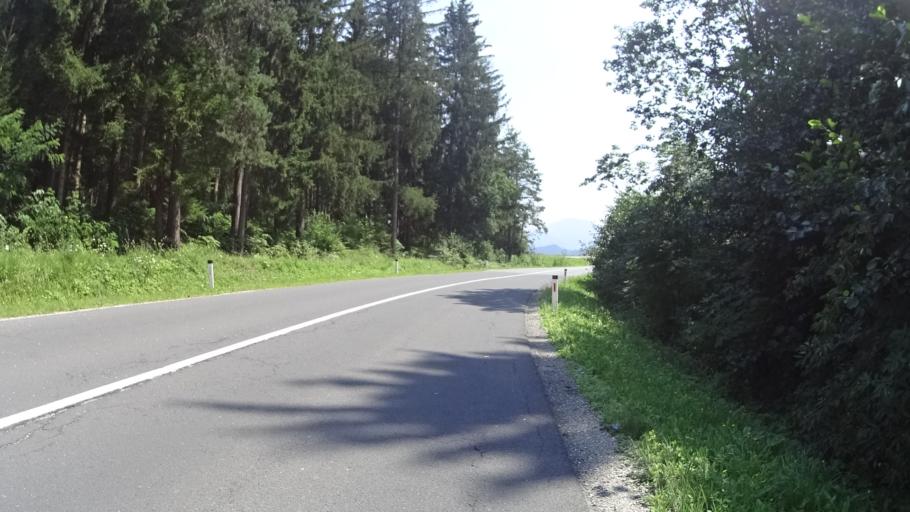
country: SI
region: Mezica
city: Mezica
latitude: 46.5638
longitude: 14.8497
